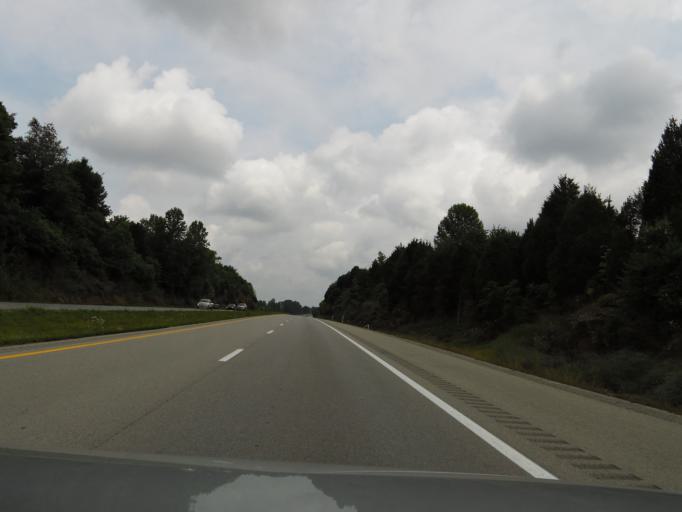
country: US
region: Kentucky
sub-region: Grayson County
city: Leitchfield
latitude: 37.5172
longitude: -86.1490
